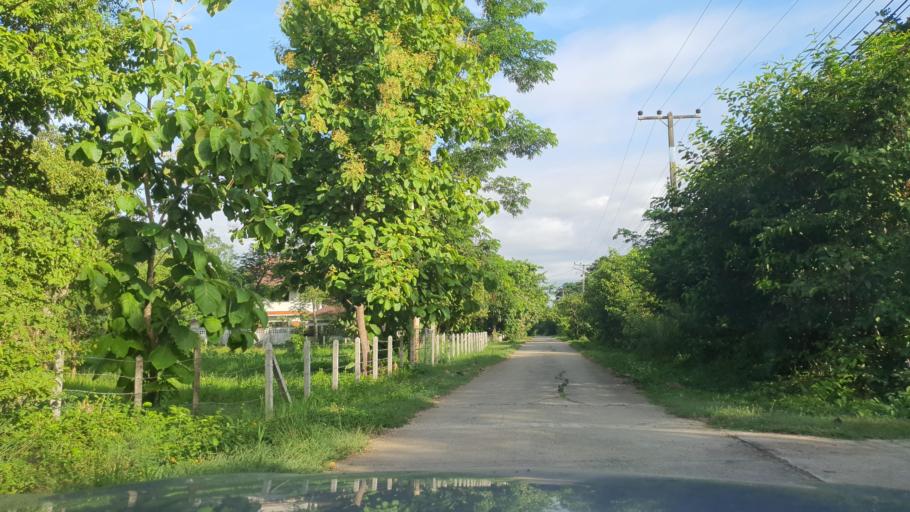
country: TH
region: Chiang Mai
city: San Kamphaeng
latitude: 18.7485
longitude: 99.1039
